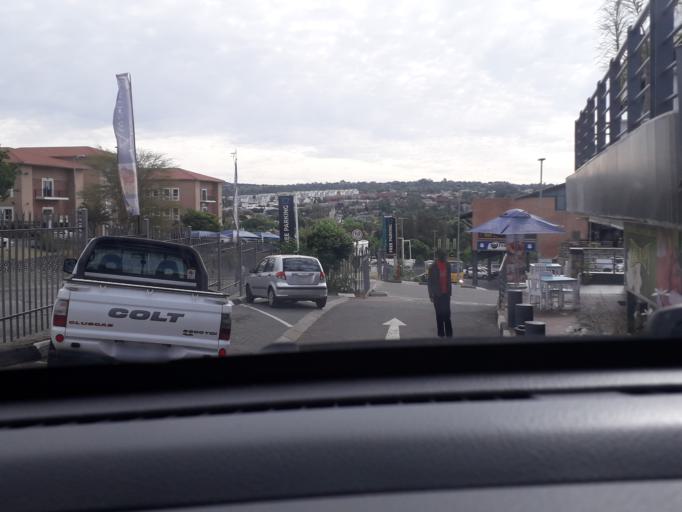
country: ZA
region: Gauteng
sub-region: City of Johannesburg Metropolitan Municipality
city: Midrand
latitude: -26.0328
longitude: 28.0630
